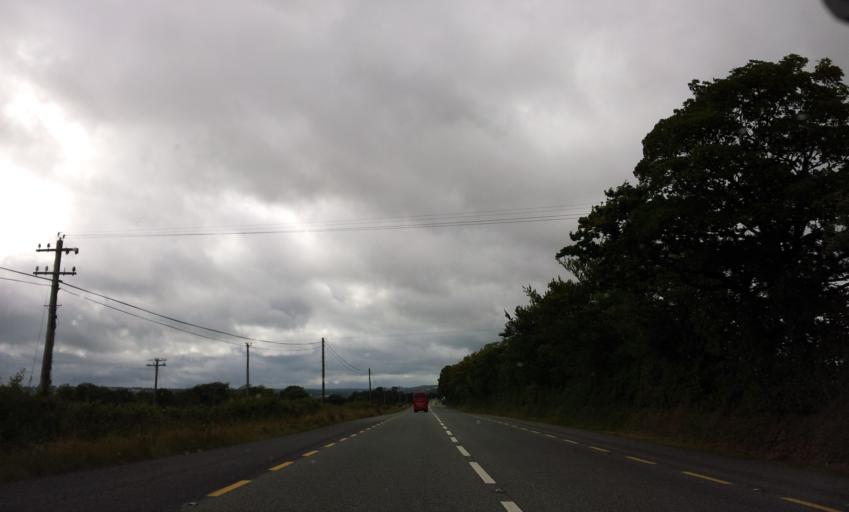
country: IE
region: Munster
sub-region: County Cork
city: Youghal
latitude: 51.9723
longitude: -7.7908
